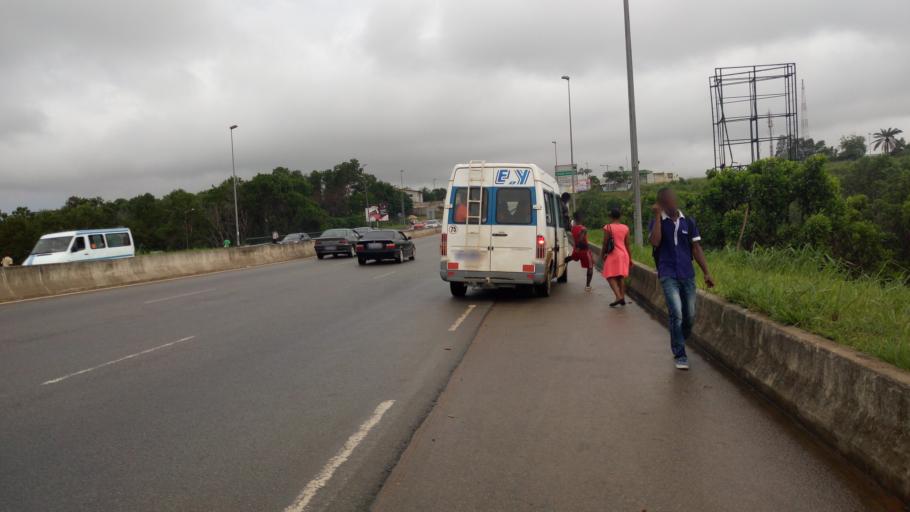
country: CI
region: Lagunes
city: Abidjan
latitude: 5.3521
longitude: -3.9826
